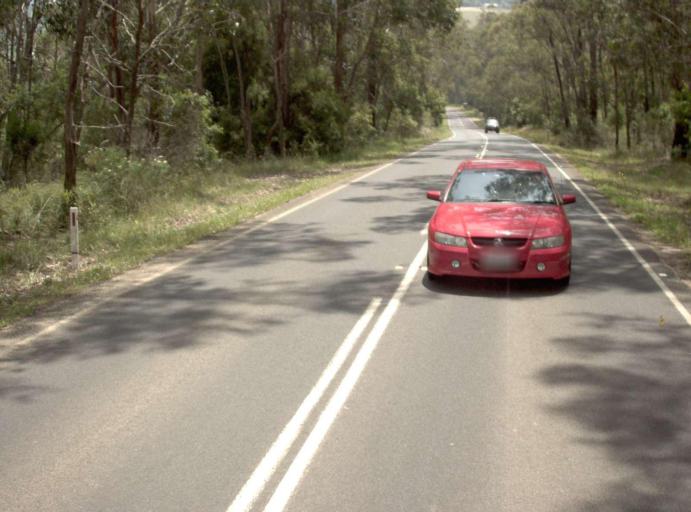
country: AU
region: Victoria
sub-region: Latrobe
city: Traralgon
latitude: -38.3979
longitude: 146.7489
